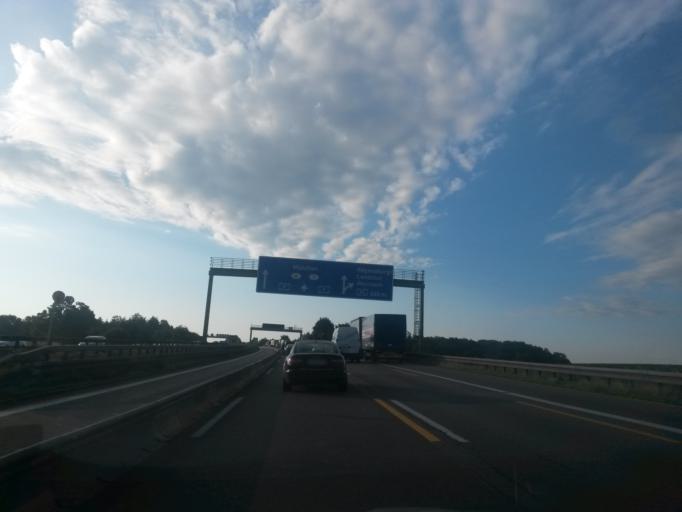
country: DE
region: Bavaria
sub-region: Upper Bavaria
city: Rohrbach
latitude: 48.5858
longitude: 11.5751
